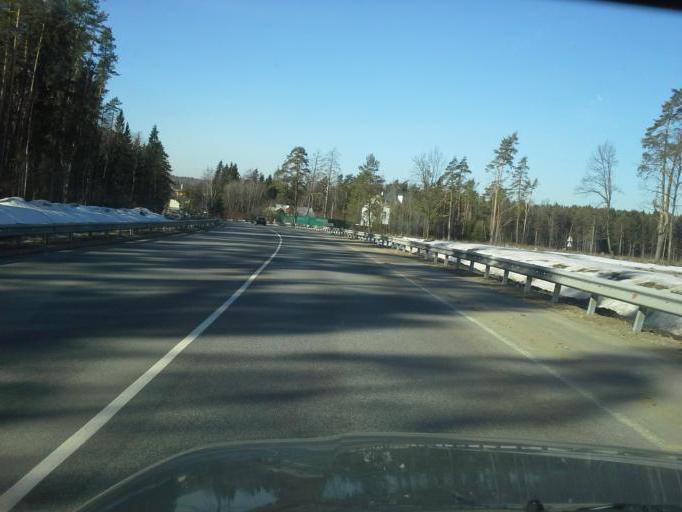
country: RU
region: Moskovskaya
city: Gorki Vtoryye
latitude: 55.6792
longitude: 37.1633
